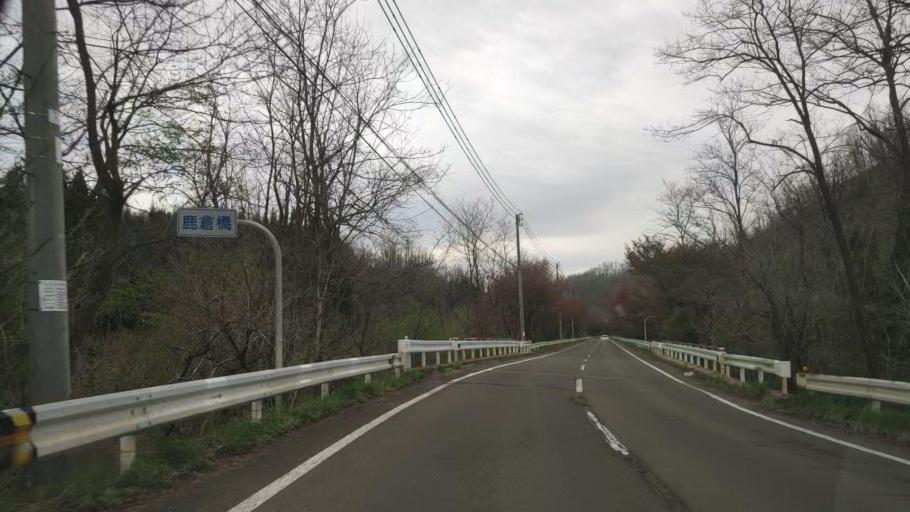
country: JP
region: Akita
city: Hanawa
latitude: 40.3461
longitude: 140.7740
